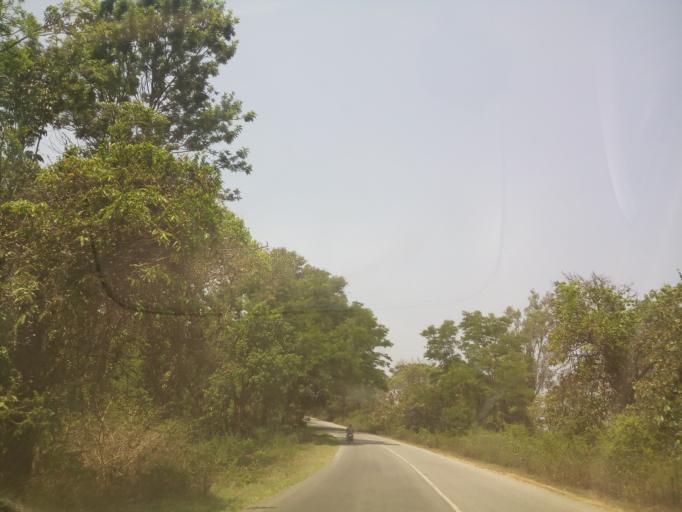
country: IN
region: Karnataka
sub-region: Hassan
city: Sakleshpur
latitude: 12.9540
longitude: 75.8646
